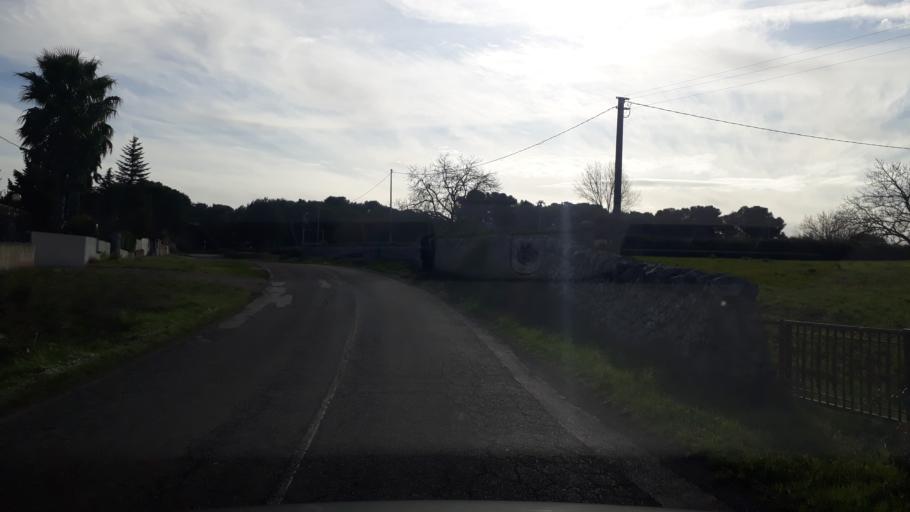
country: IT
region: Apulia
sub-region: Provincia di Taranto
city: Martina Franca
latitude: 40.6725
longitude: 17.3631
